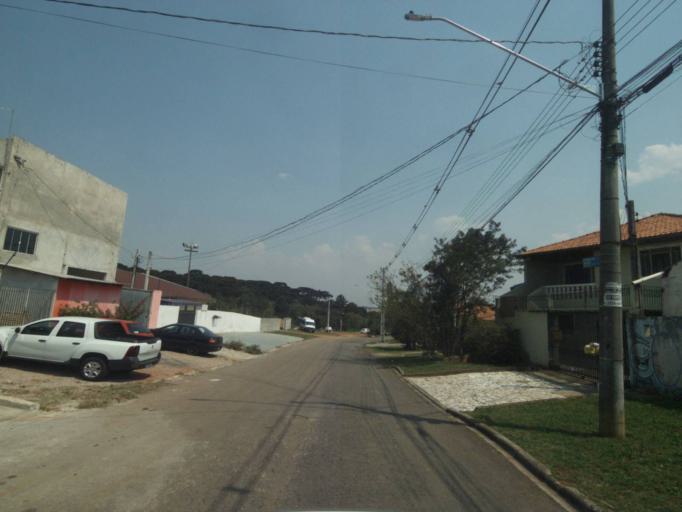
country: BR
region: Parana
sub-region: Sao Jose Dos Pinhais
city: Sao Jose dos Pinhais
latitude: -25.5450
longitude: -49.2430
